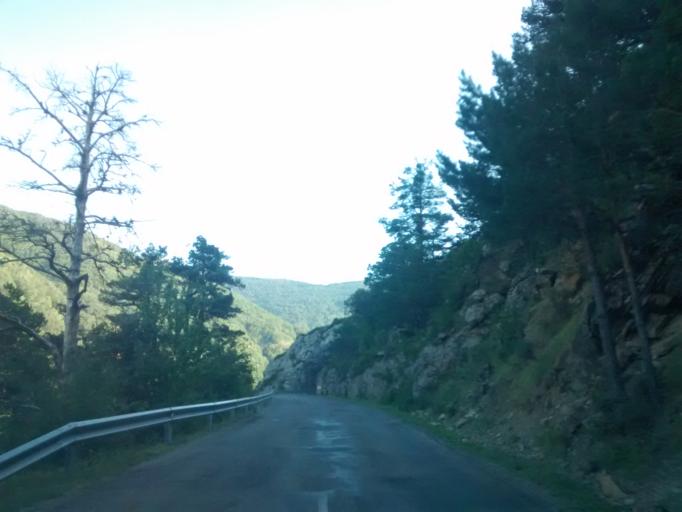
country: ES
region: Aragon
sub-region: Provincia de Huesca
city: Anso
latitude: 42.7874
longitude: -0.7372
